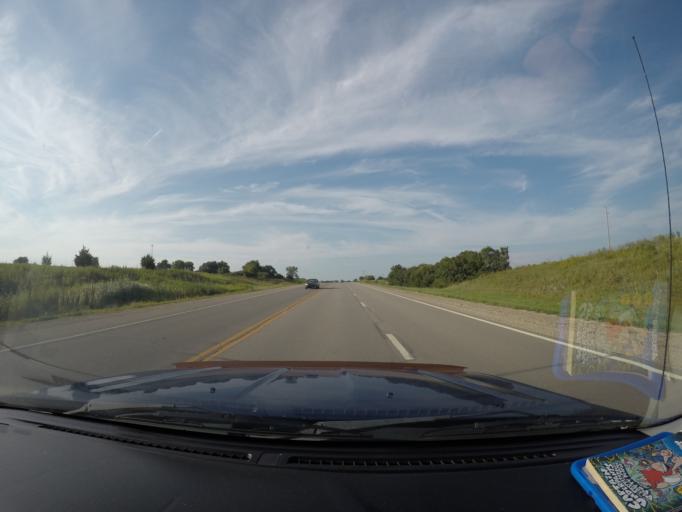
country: US
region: Kansas
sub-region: Atchison County
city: Atchison
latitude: 39.5287
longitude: -95.1329
